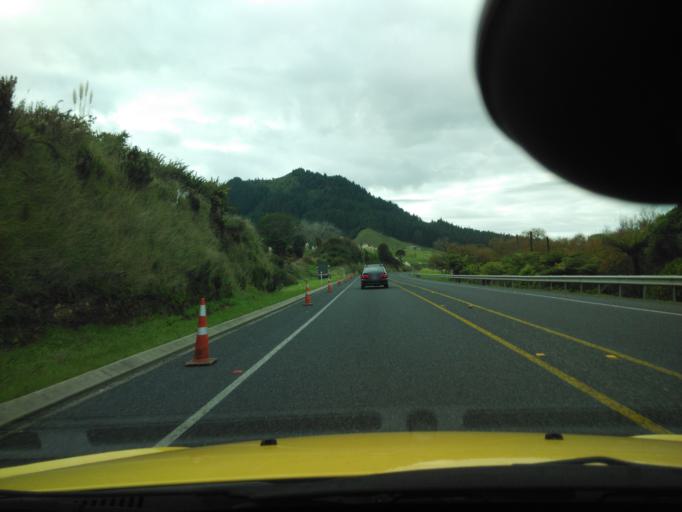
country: NZ
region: Waikato
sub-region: Waikato District
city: Ngaruawahia
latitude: -37.6010
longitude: 175.1684
